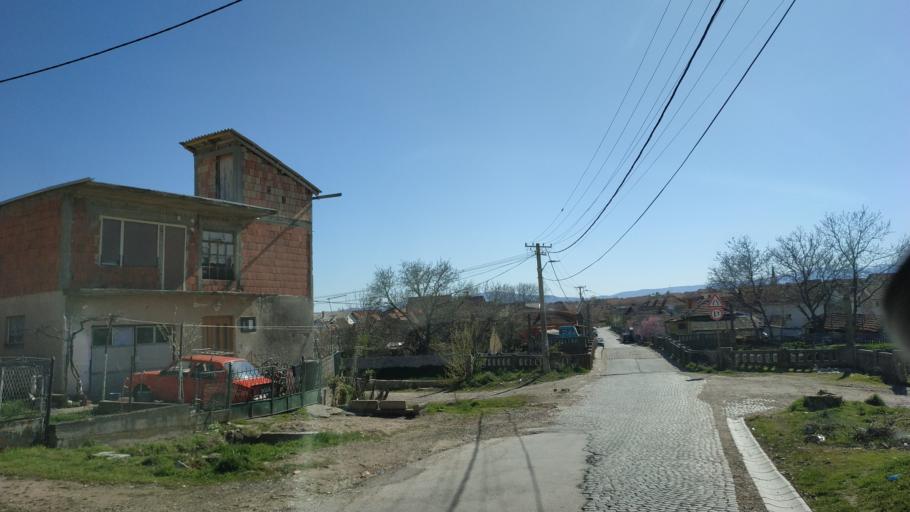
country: RS
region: Central Serbia
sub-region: Nisavski Okrug
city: Aleksinac
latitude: 43.5466
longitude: 21.7135
